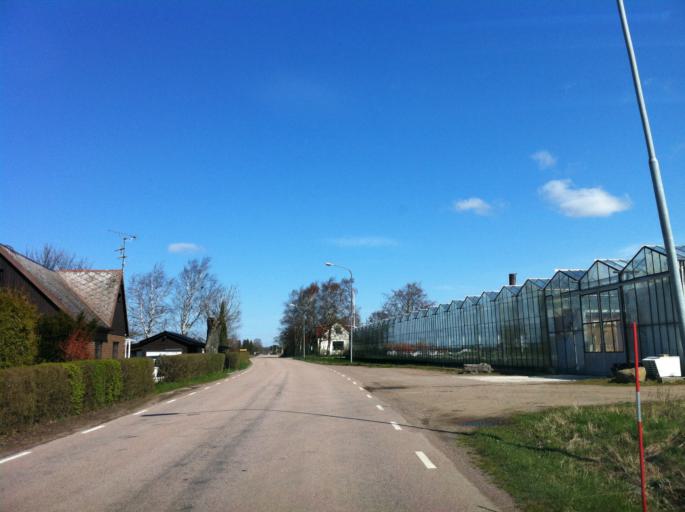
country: SE
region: Skane
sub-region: Helsingborg
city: Glumslov
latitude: 55.9594
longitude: 12.8269
